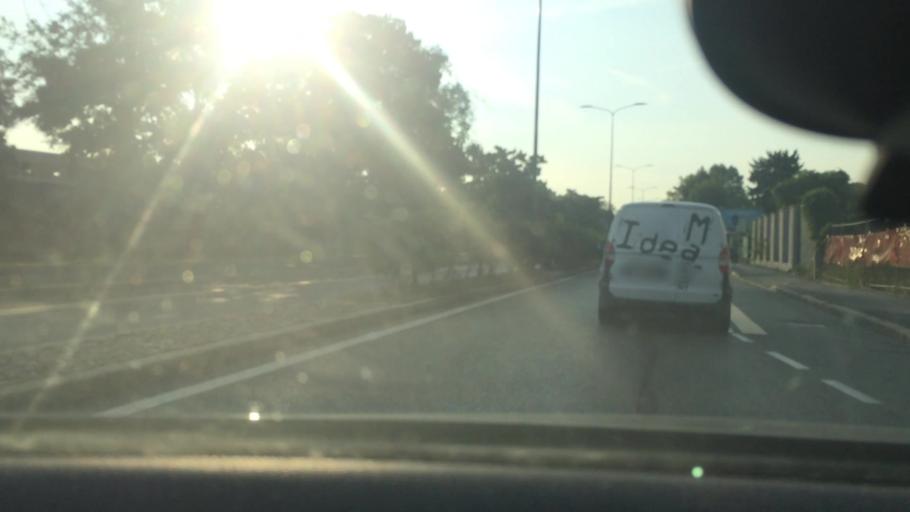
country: IT
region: Lombardy
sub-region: Citta metropolitana di Milano
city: Baranzate
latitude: 45.5024
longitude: 9.1156
